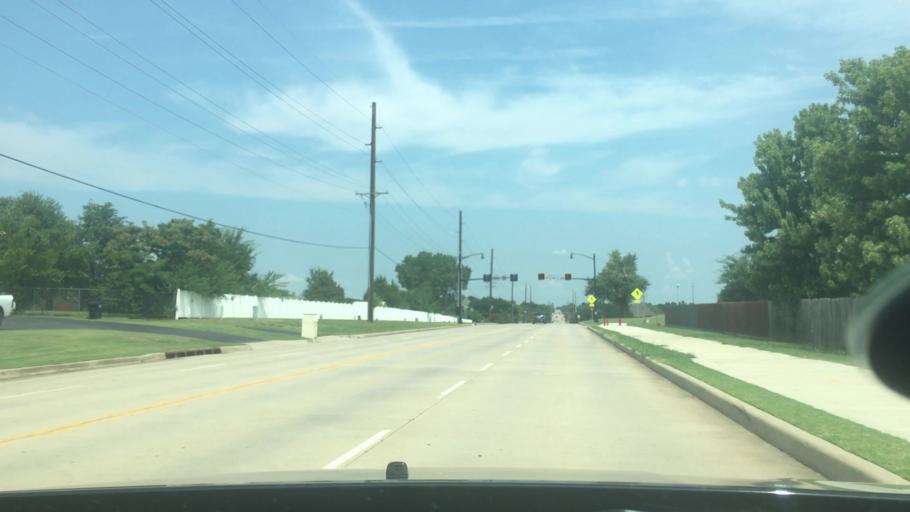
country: US
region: Oklahoma
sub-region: Pottawatomie County
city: Shawnee
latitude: 35.3357
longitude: -96.8943
